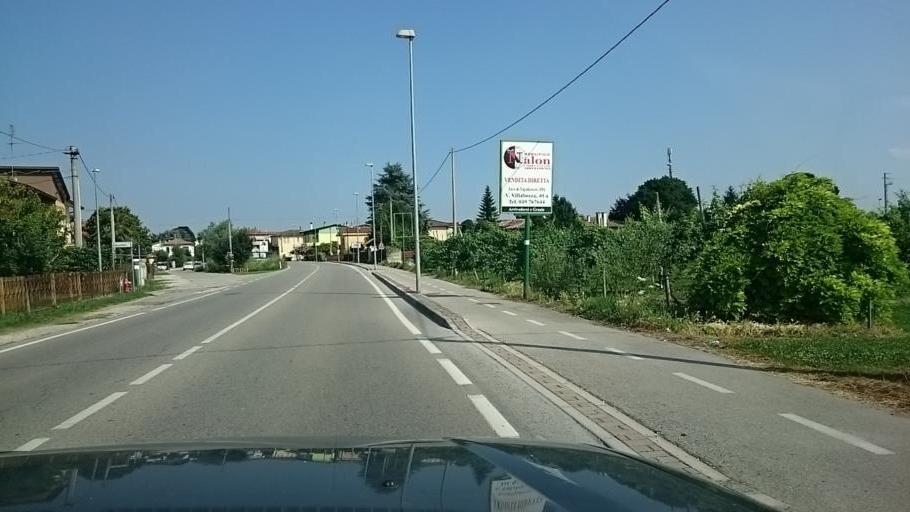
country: IT
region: Veneto
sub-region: Provincia di Padova
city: Vigodarzere
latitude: 45.4621
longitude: 11.8738
